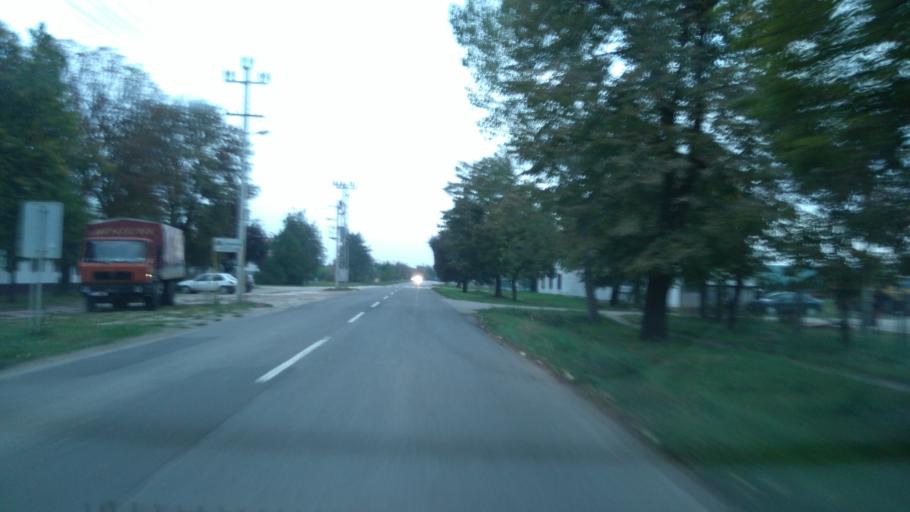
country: RS
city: Mol
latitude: 45.7846
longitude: 20.1363
